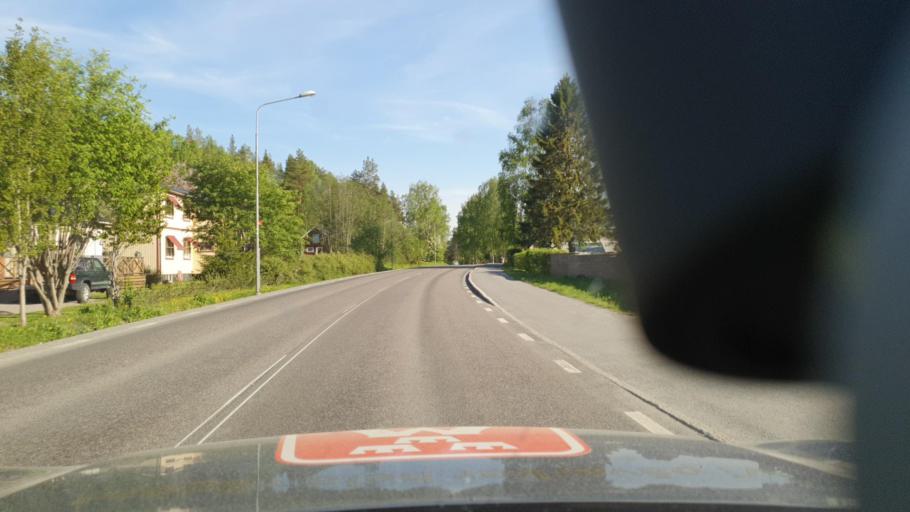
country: SE
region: Norrbotten
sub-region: Bodens Kommun
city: Boden
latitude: 65.8374
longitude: 21.6117
